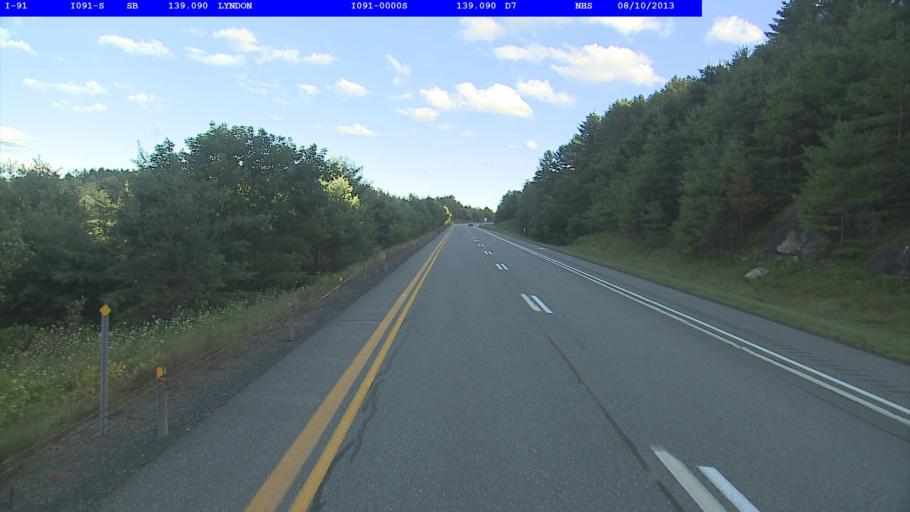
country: US
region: Vermont
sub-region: Caledonia County
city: Lyndonville
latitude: 44.5428
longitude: -72.0231
